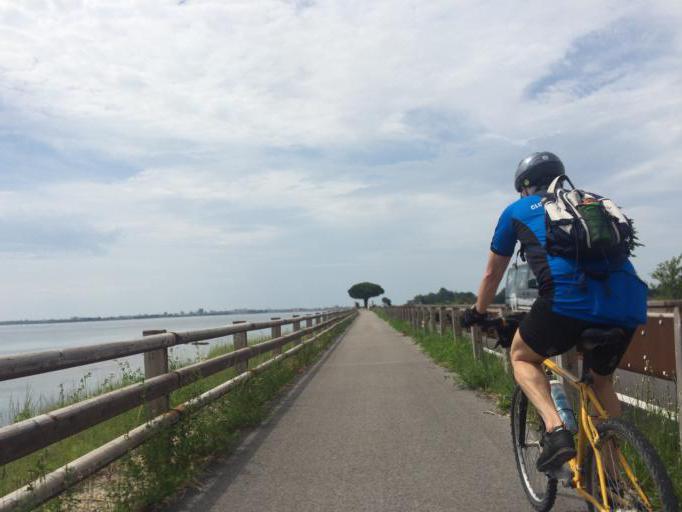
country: IT
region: Friuli Venezia Giulia
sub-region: Provincia di Gorizia
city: Grado
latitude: 45.7169
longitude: 13.3851
